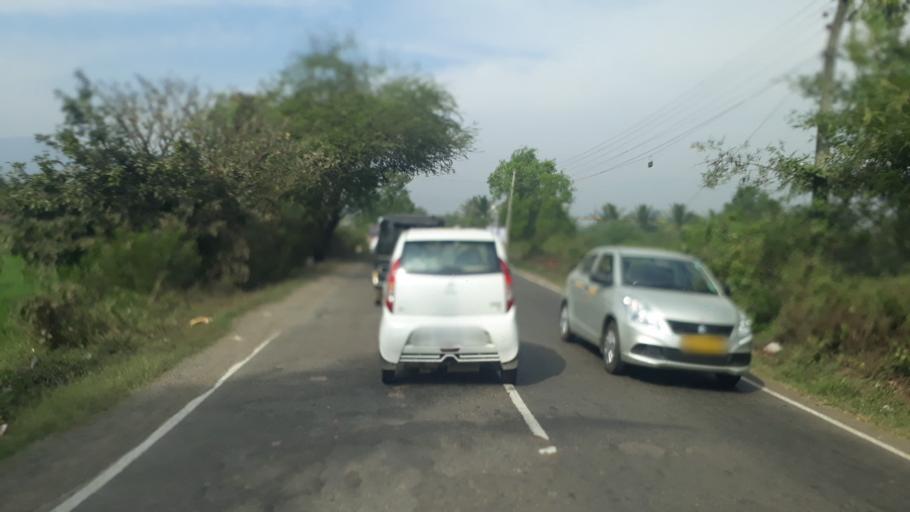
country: IN
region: Maharashtra
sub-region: Raigarh
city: Alibag
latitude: 18.6878
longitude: 72.9818
